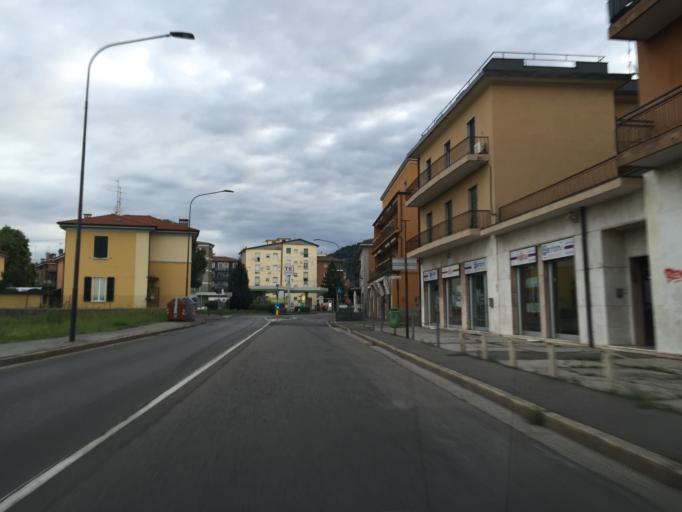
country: IT
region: Lombardy
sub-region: Provincia di Brescia
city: Brescia
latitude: 45.5220
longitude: 10.2297
